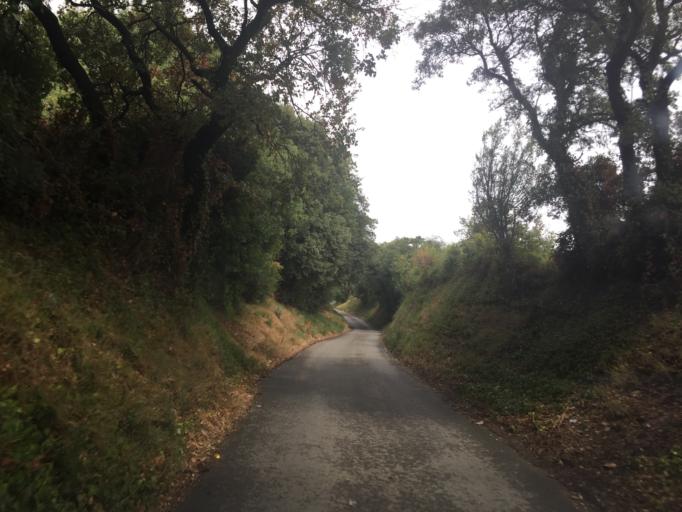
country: FR
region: Provence-Alpes-Cote d'Azur
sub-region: Departement du Vaucluse
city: Chateauneuf-du-Pape
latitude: 44.0634
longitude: 4.8332
